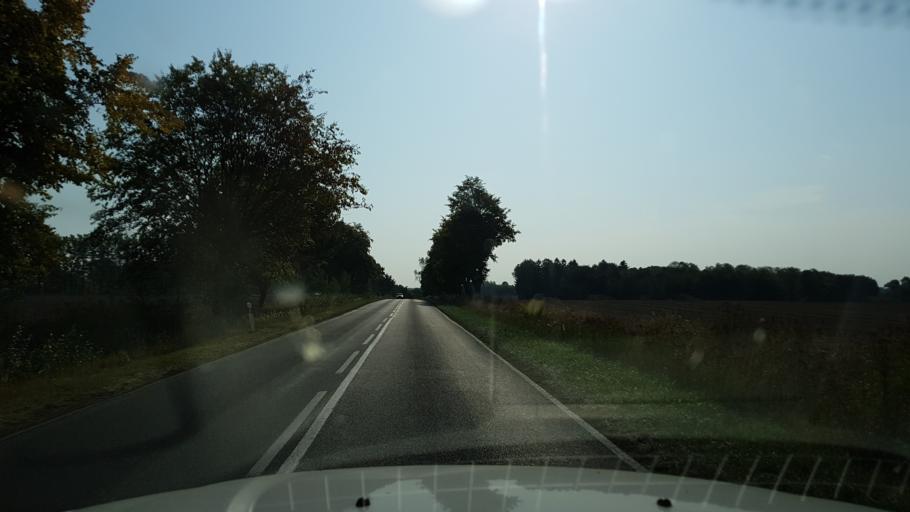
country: PL
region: West Pomeranian Voivodeship
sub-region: Powiat gryficki
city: Ploty
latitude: 53.7913
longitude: 15.2924
